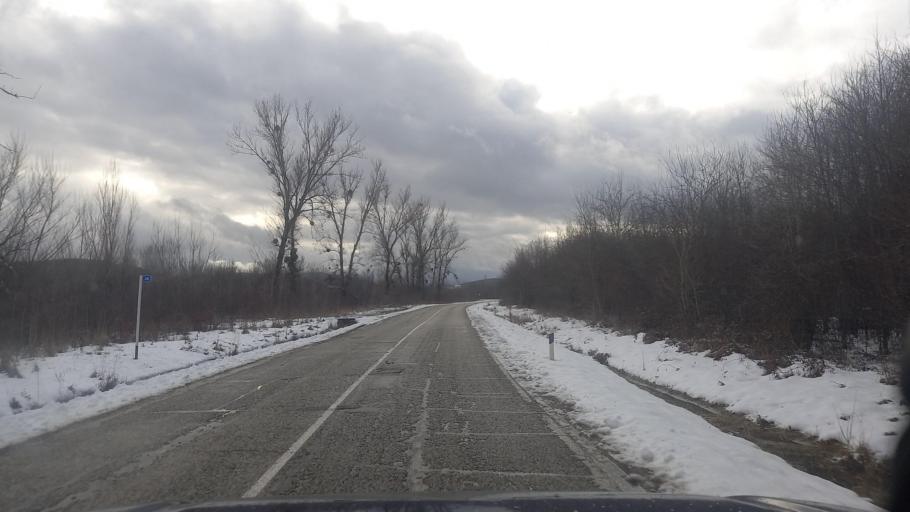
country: RU
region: Krasnodarskiy
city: Smolenskaya
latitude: 44.7576
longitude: 38.8467
